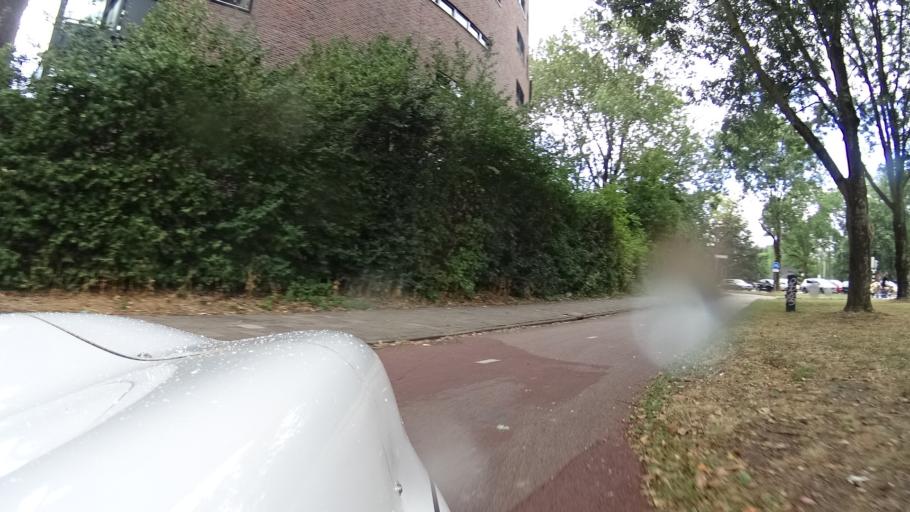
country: NL
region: Utrecht
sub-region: Gemeente Utrecht
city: Utrecht
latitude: 52.1019
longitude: 5.1427
